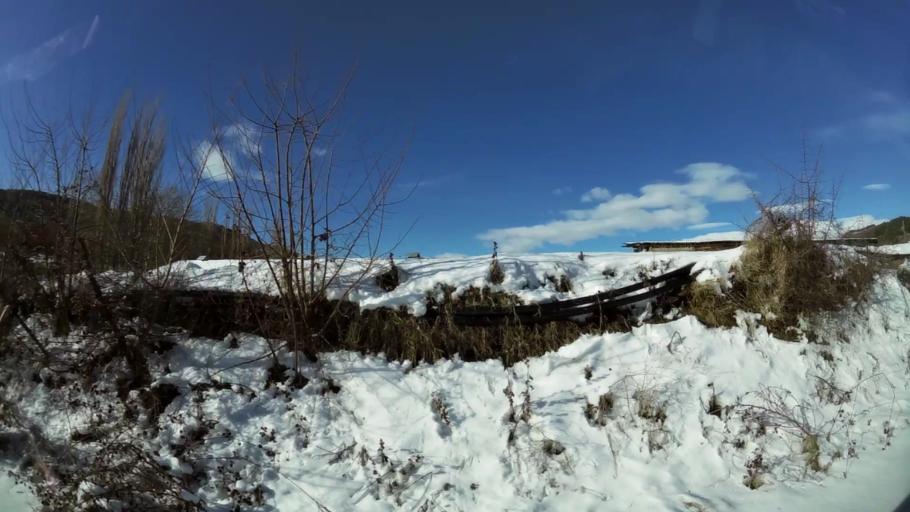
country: MK
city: Ljubin
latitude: 41.9859
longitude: 21.2975
